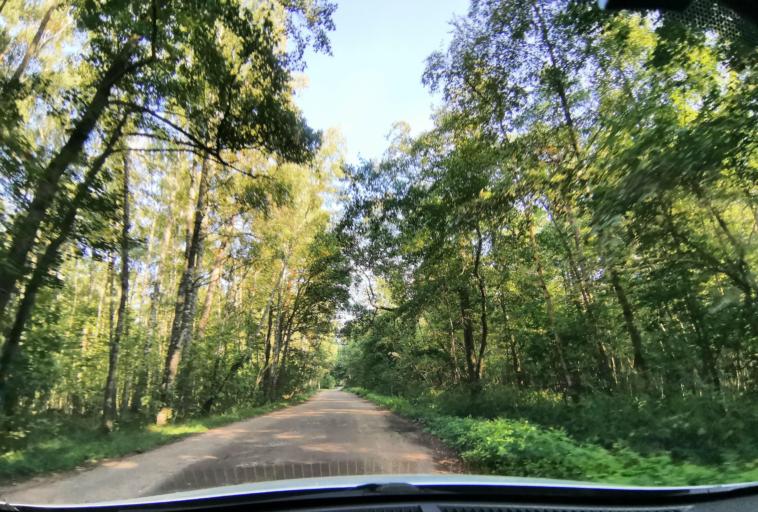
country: LT
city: Nida
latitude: 55.1589
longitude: 20.8391
